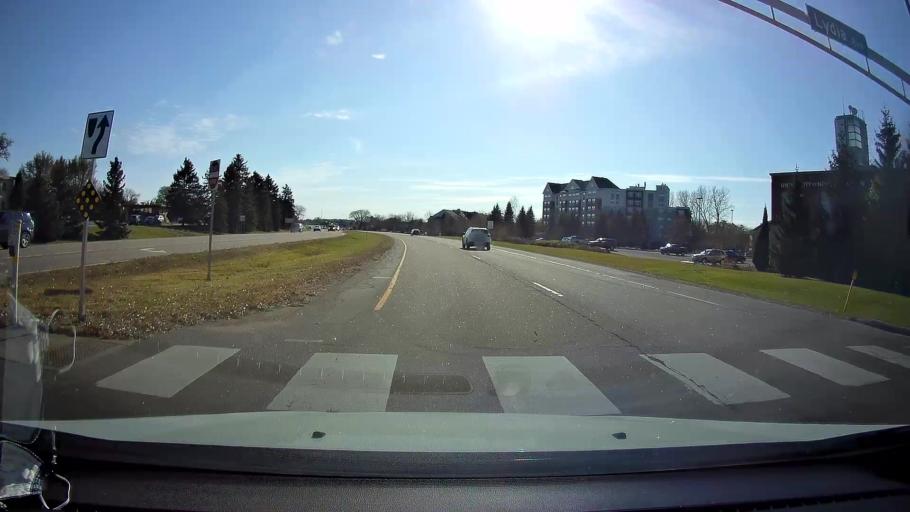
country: US
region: Minnesota
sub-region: Ramsey County
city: Arden Hills
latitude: 45.0313
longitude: -93.1667
